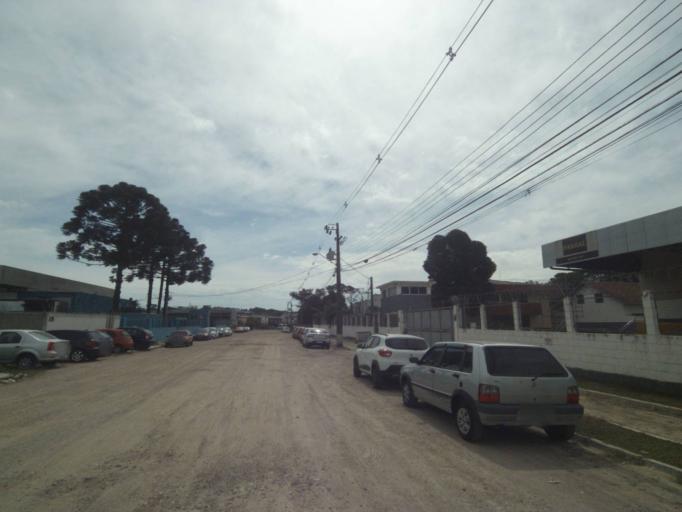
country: BR
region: Parana
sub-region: Araucaria
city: Araucaria
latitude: -25.5186
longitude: -49.3320
